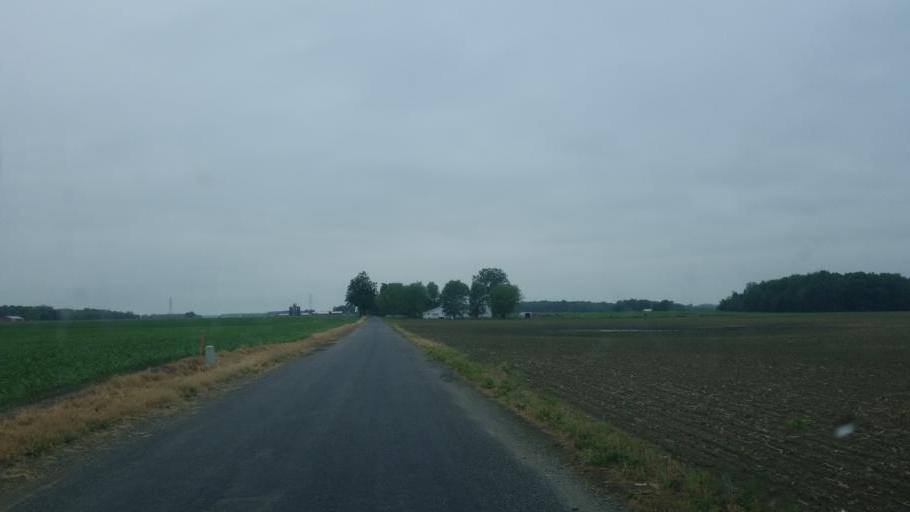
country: US
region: Indiana
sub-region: Marshall County
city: Bremen
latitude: 41.4937
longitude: -86.1233
